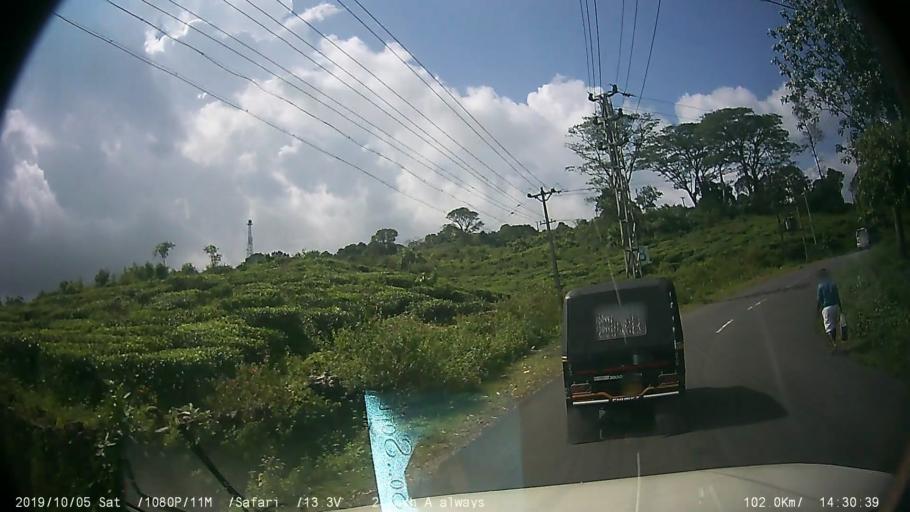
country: IN
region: Kerala
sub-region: Kottayam
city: Erattupetta
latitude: 9.6114
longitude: 76.9687
